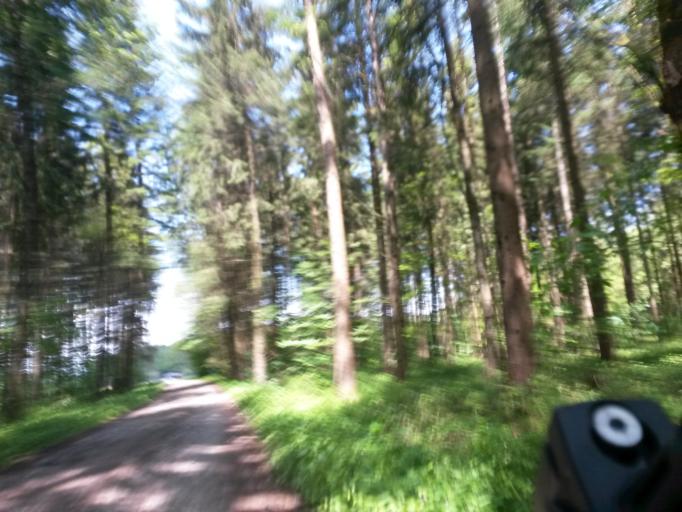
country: DE
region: Baden-Wuerttemberg
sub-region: Tuebingen Region
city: Aulendorf
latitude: 47.9509
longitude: 9.6789
